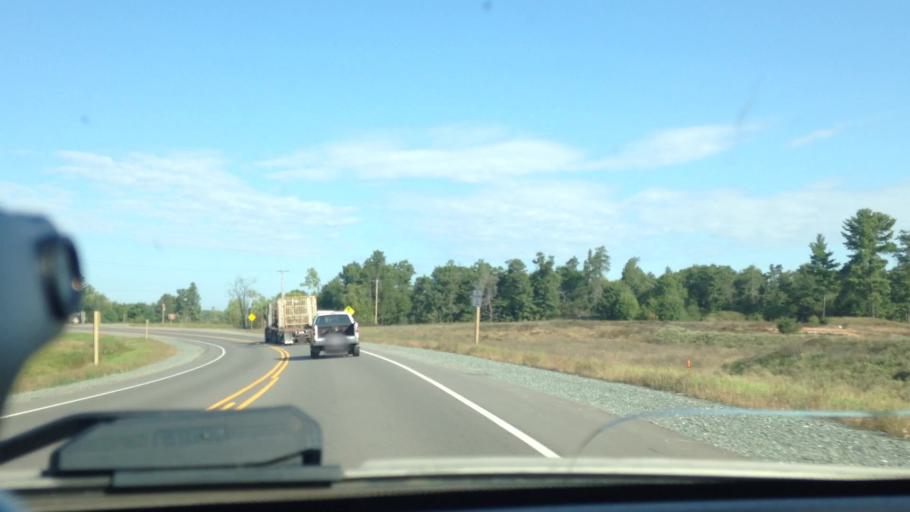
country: US
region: Michigan
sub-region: Dickinson County
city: Iron Mountain
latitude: 45.8736
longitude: -88.0848
